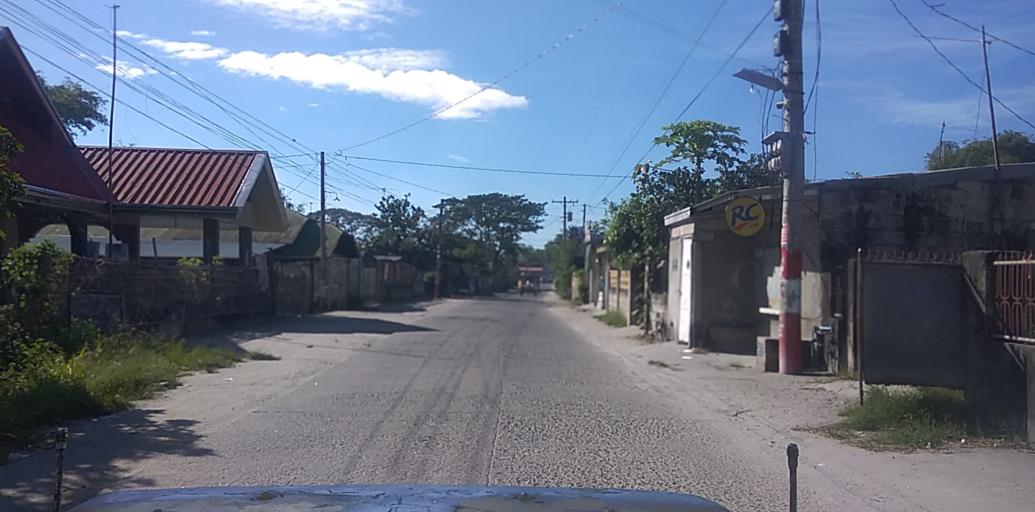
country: PH
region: Central Luzon
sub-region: Province of Pampanga
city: San Patricio
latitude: 15.0946
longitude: 120.7134
